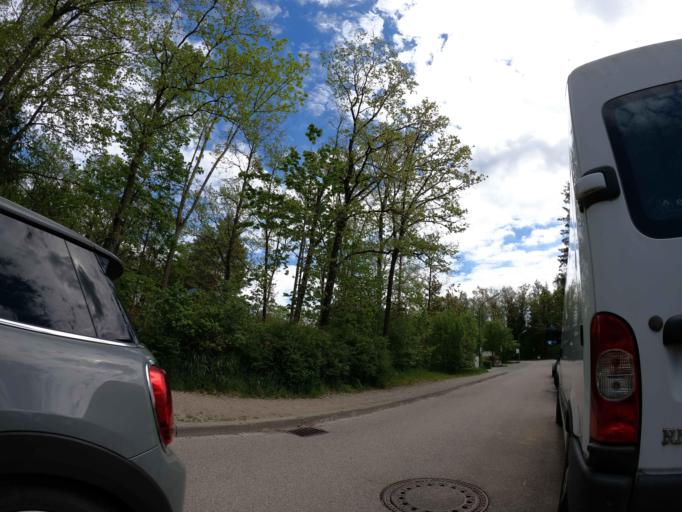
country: DE
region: Bavaria
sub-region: Upper Bavaria
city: Ottobrunn
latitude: 48.0663
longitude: 11.6801
